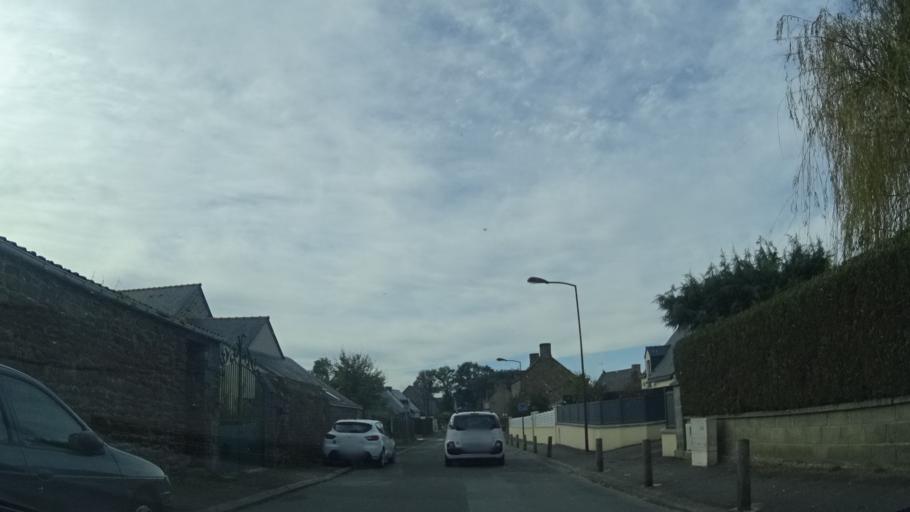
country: FR
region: Brittany
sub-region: Departement d'Ille-et-Vilaine
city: Bonnemain
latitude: 48.4666
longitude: -1.7682
